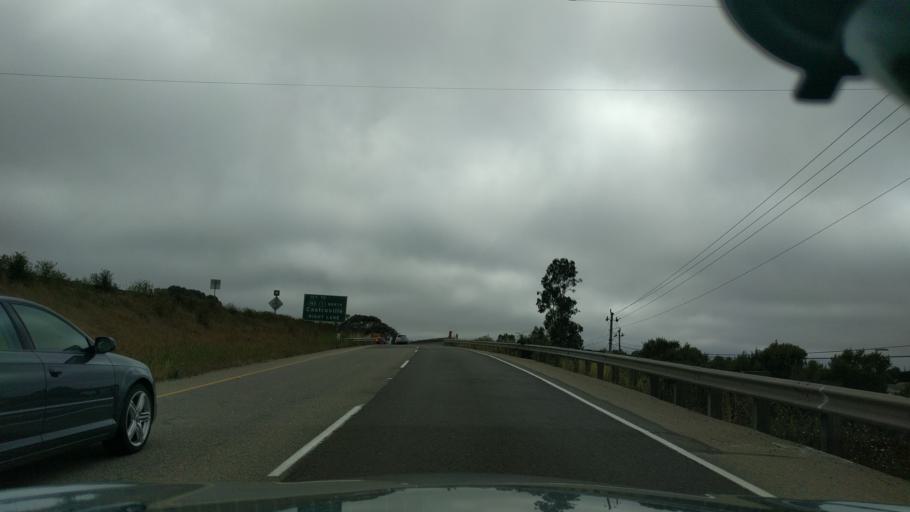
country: US
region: California
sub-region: Monterey County
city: Castroville
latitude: 36.7678
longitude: -121.7457
